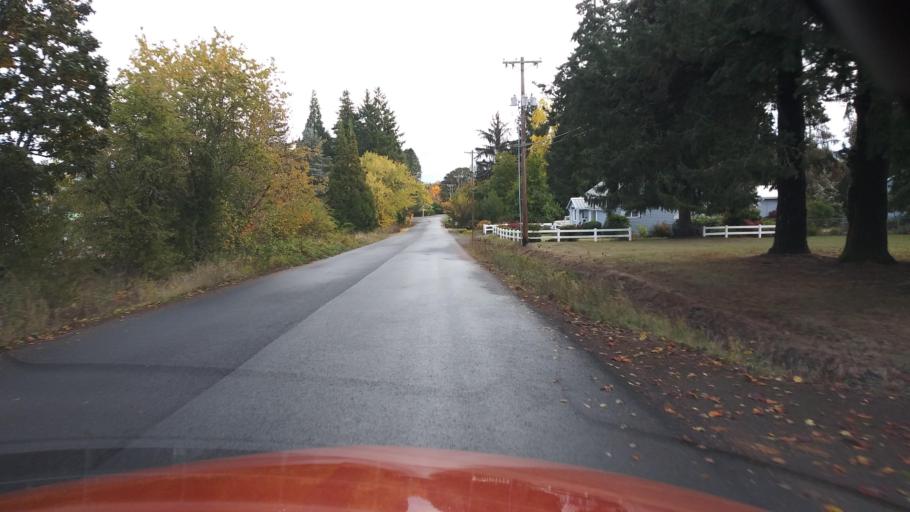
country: US
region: Oregon
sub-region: Washington County
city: Forest Grove
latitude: 45.5325
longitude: -123.1313
